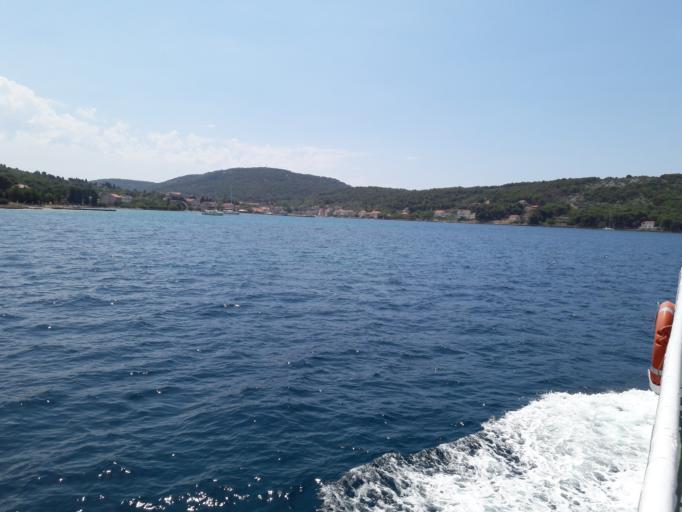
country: HR
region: Sibensko-Kniniska
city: Vodice
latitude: 43.7058
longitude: 15.8306
